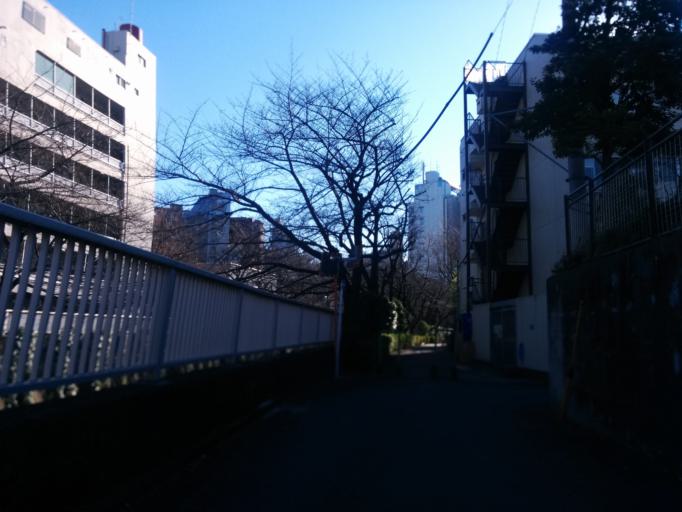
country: JP
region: Tokyo
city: Tokyo
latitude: 35.7115
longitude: 139.6943
